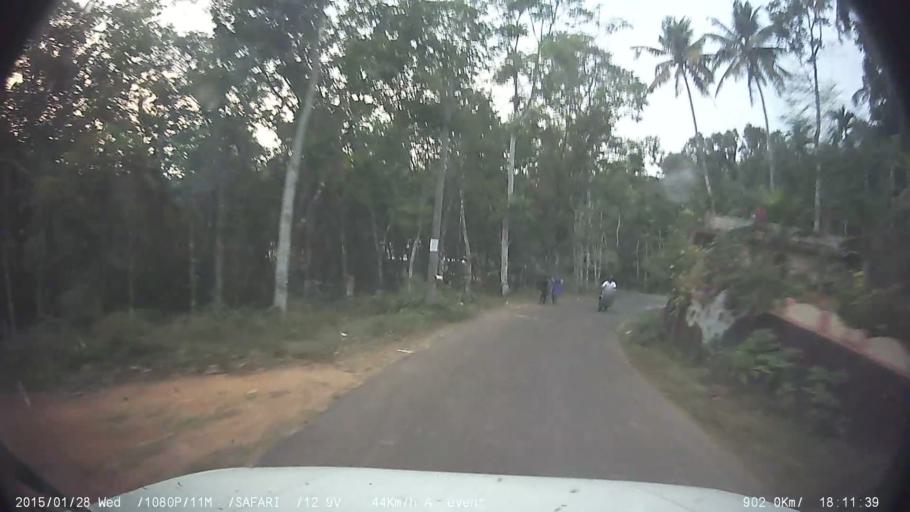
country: IN
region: Kerala
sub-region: Kottayam
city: Palackattumala
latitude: 9.7520
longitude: 76.5683
